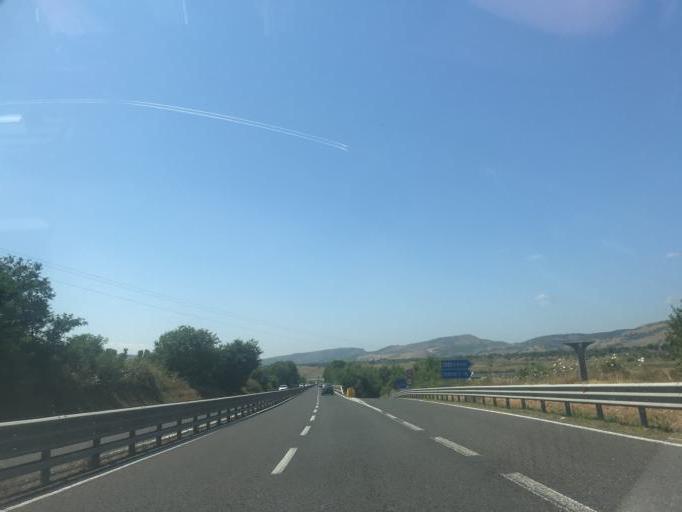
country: IT
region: Sardinia
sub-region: Provincia di Sassari
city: Florinas
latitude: 40.6686
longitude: 8.6655
